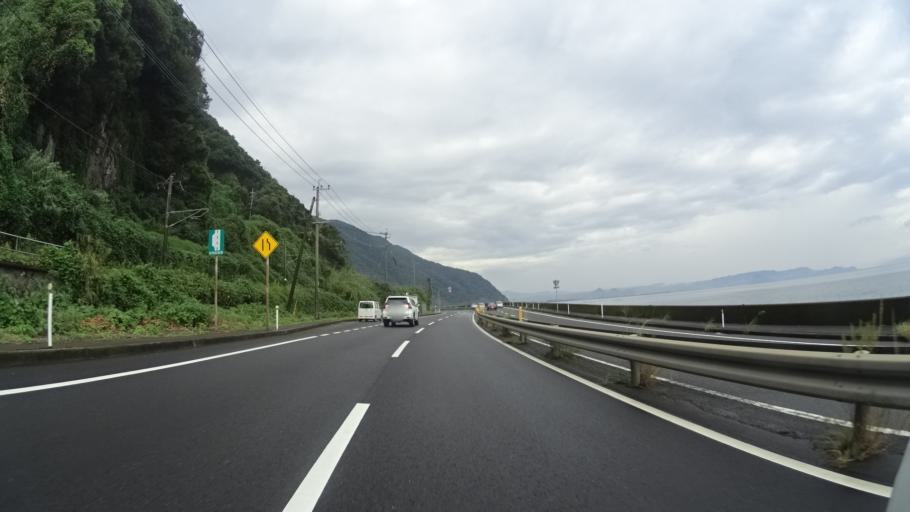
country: JP
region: Kagoshima
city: Kajiki
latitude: 31.6735
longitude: 130.6110
